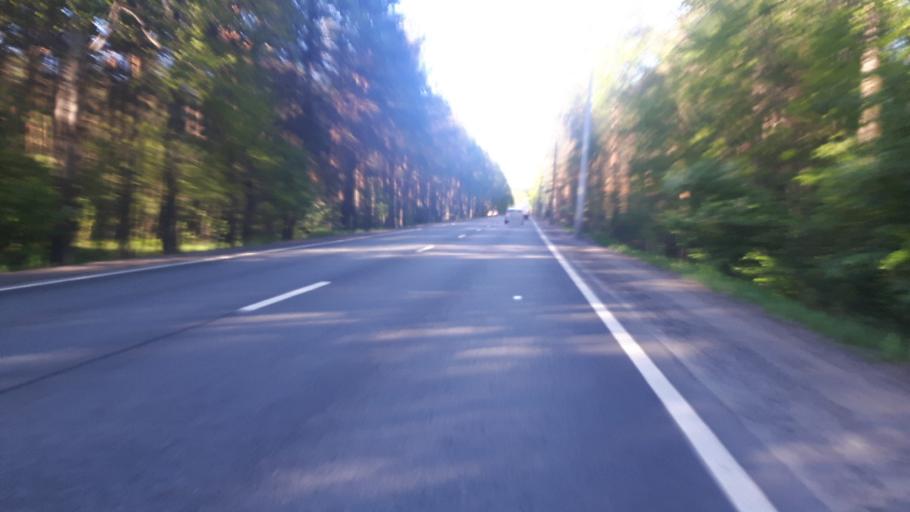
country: RU
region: Leningrad
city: Molodezhnoye
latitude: 60.1766
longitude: 29.4437
